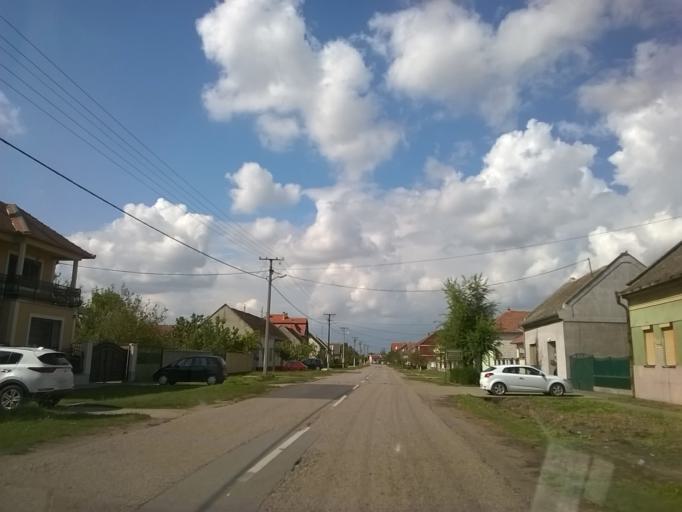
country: RS
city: Lokve
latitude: 45.1552
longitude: 21.0294
